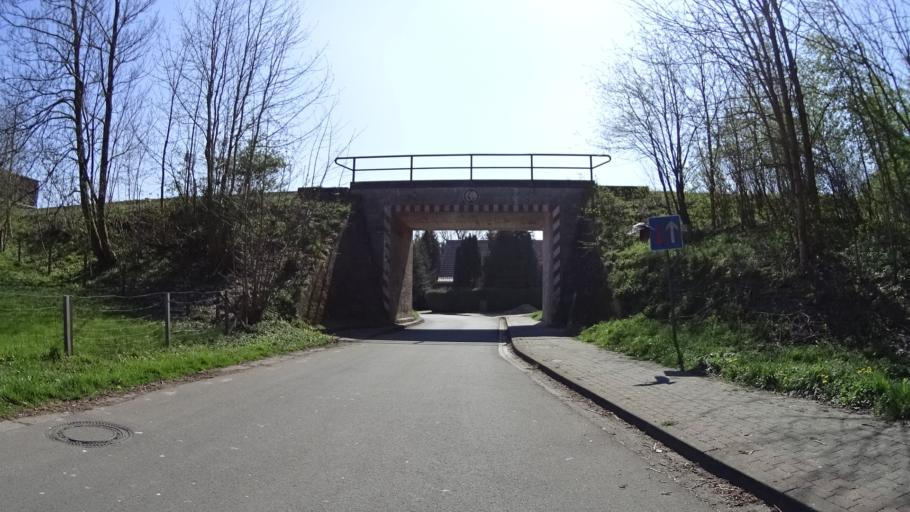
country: DE
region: Lower Saxony
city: Weener
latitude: 53.1613
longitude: 7.3703
